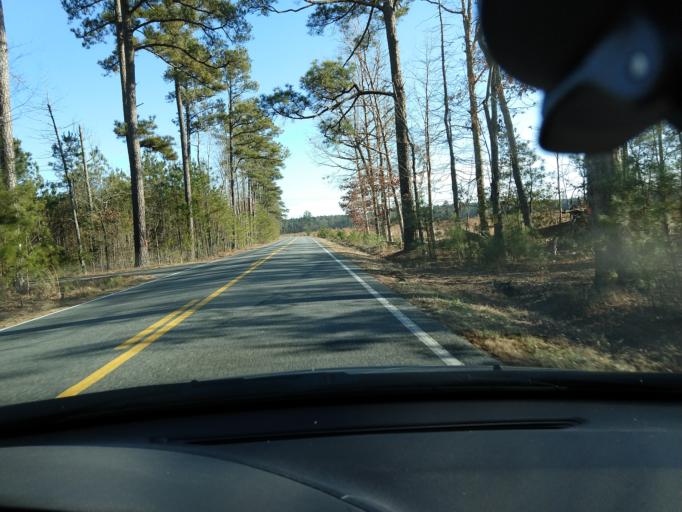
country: US
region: Virginia
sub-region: Charles City County
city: Charles City
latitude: 37.3053
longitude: -76.9579
